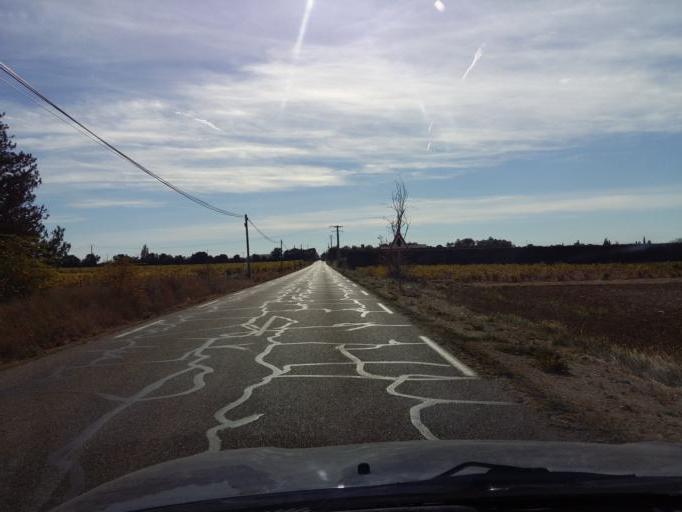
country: FR
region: Provence-Alpes-Cote d'Azur
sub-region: Departement du Vaucluse
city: Orange
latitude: 44.1738
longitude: 4.8015
